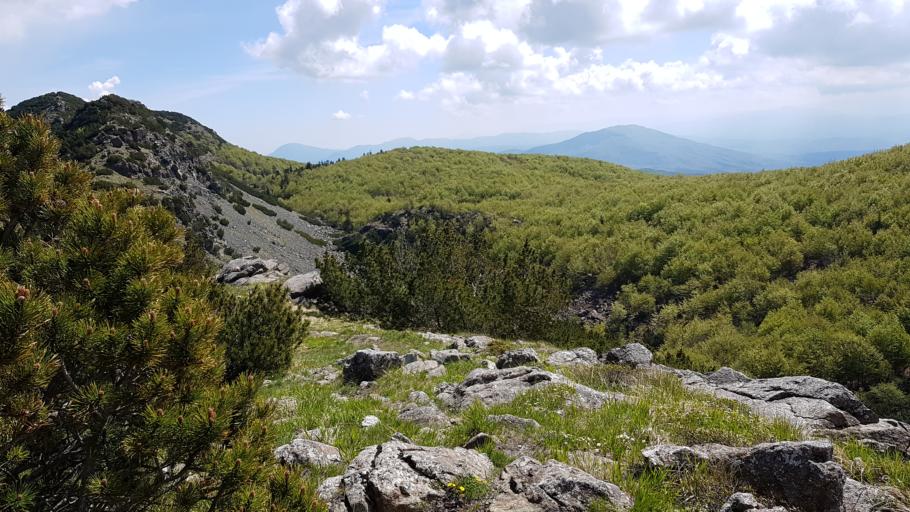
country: IT
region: Liguria
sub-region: Provincia di Genova
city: Santo Stefano d'Aveto
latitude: 44.5580
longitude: 9.5006
